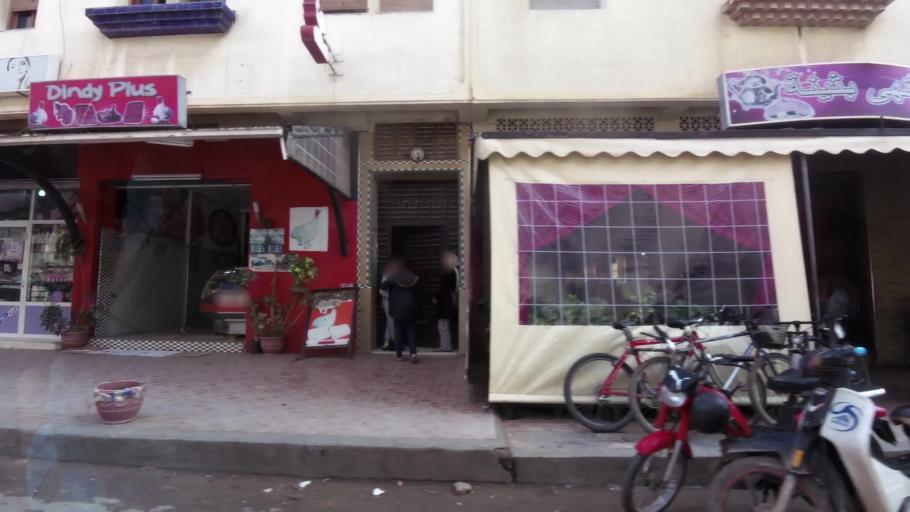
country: MA
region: Chaouia-Ouardigha
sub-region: Settat Province
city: Berrechid
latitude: 33.2649
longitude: -7.5800
